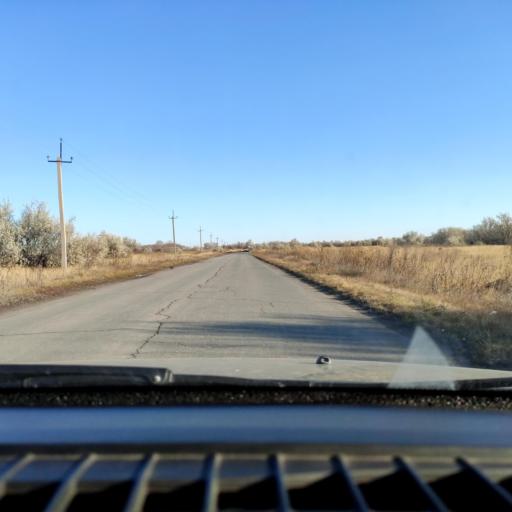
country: RU
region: Samara
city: Tol'yatti
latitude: 53.6538
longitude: 49.3269
